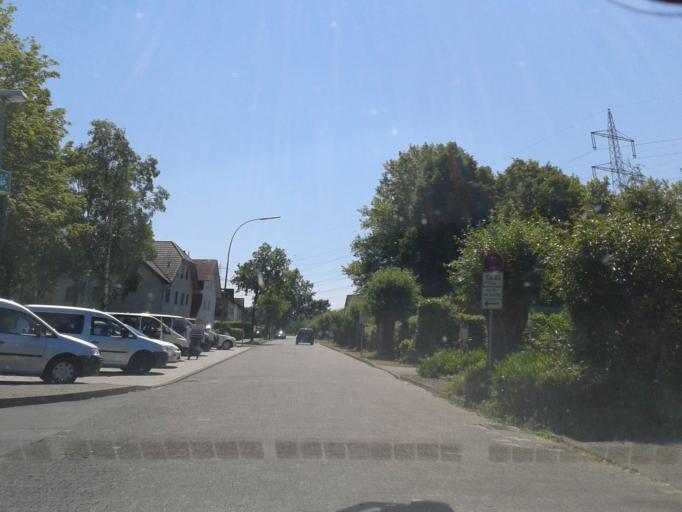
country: DE
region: North Rhine-Westphalia
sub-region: Regierungsbezirk Detmold
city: Paderborn
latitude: 51.7464
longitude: 8.7041
